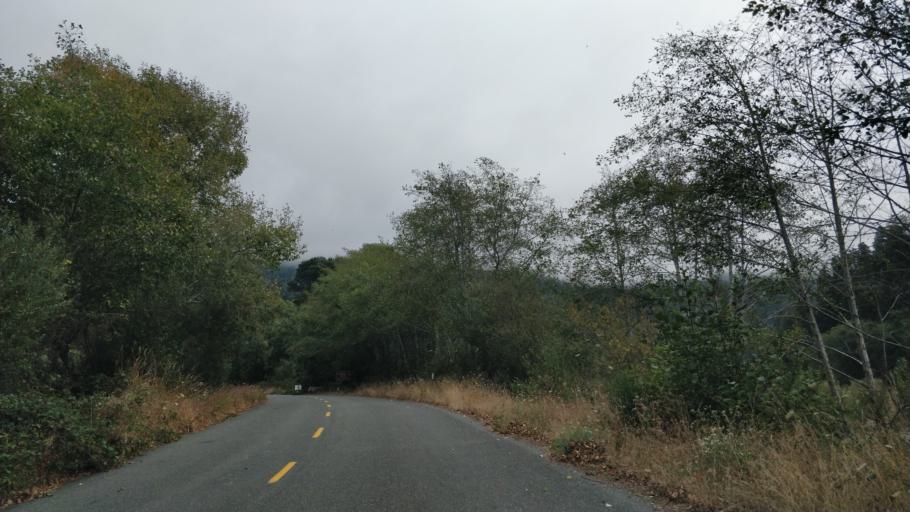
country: US
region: California
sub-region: Humboldt County
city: Westhaven-Moonstone
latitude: 41.3001
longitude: -124.0449
